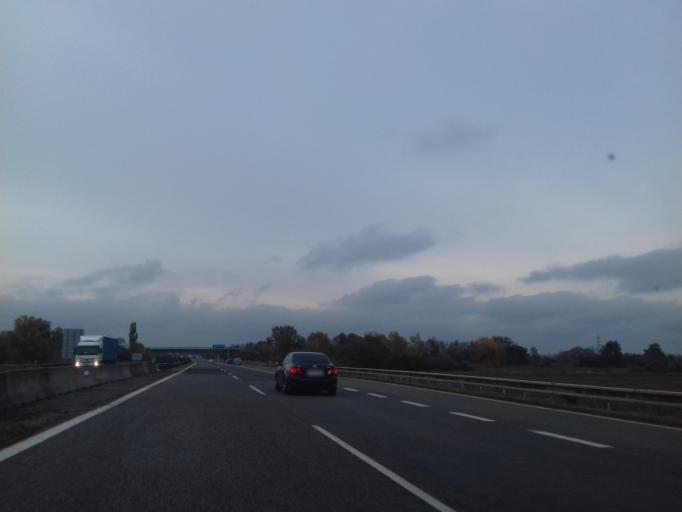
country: CZ
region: South Moravian
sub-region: Okres Breclav
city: Lanzhot
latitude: 48.6358
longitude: 17.0038
